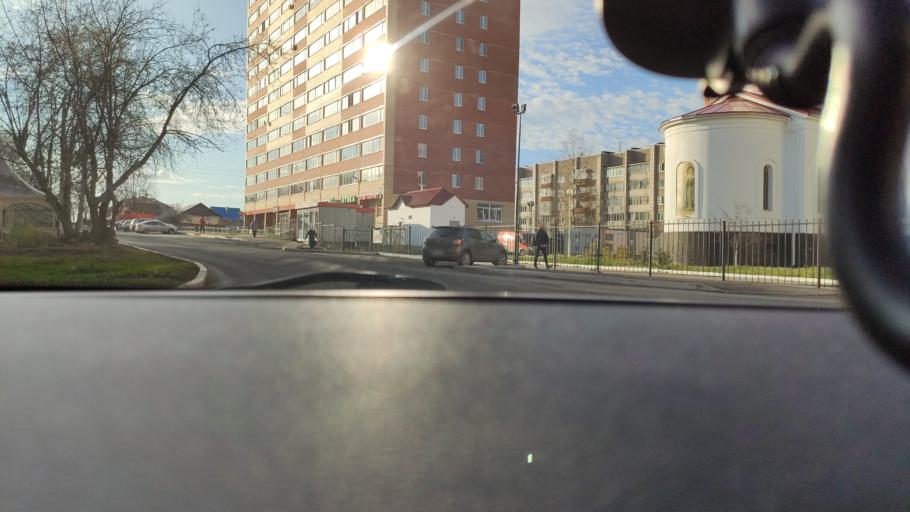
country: RU
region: Perm
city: Kondratovo
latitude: 58.0487
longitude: 56.0872
